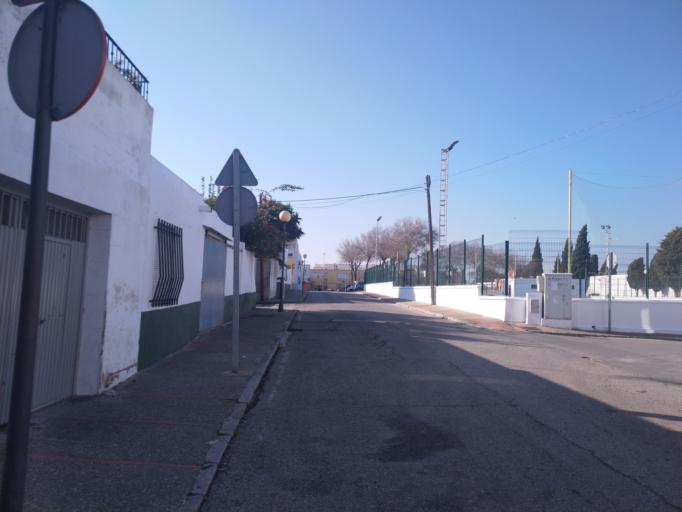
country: ES
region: Andalusia
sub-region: Provincia de Cadiz
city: San Fernando
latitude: 36.4696
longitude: -6.2021
